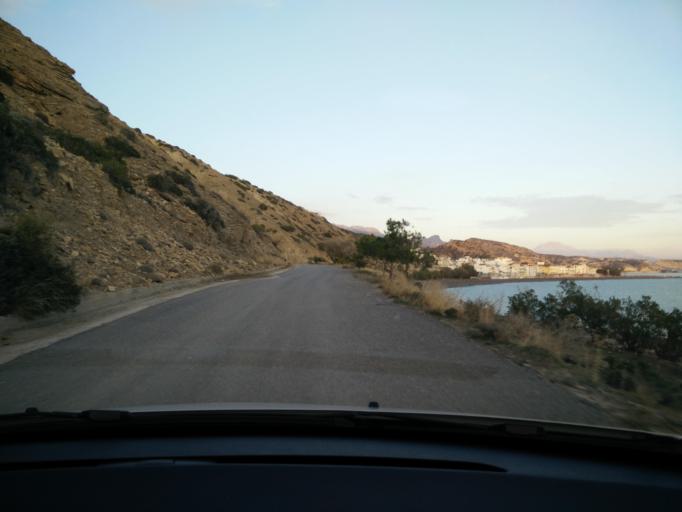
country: GR
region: Crete
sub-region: Nomos Lasithiou
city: Gra Liyia
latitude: 35.0018
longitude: 25.5784
